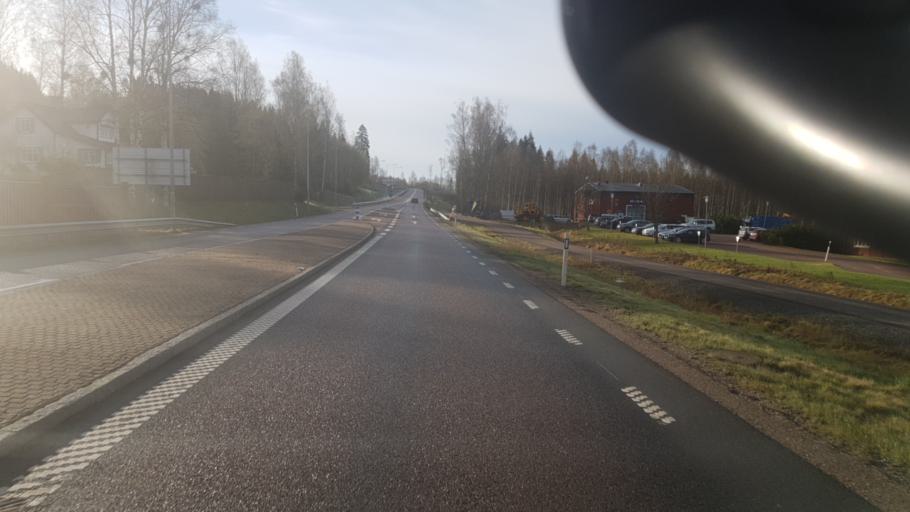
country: SE
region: Vaermland
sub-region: Eda Kommun
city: Amotfors
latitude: 59.7699
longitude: 12.3803
